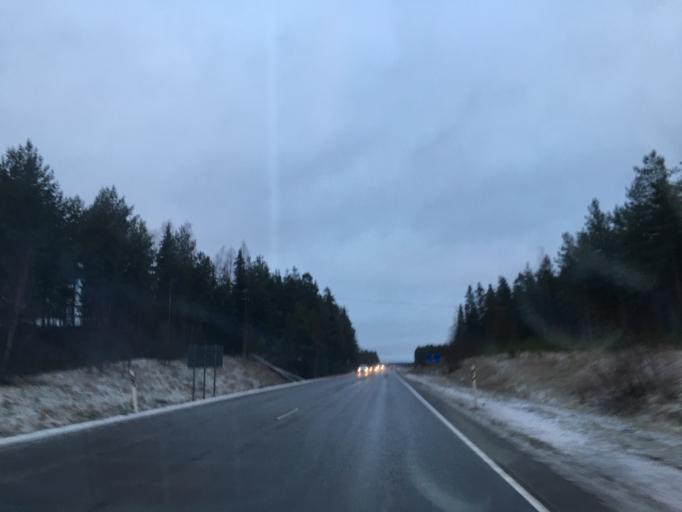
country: FI
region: Varsinais-Suomi
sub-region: Loimaa
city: Aura
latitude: 60.6513
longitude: 22.5525
